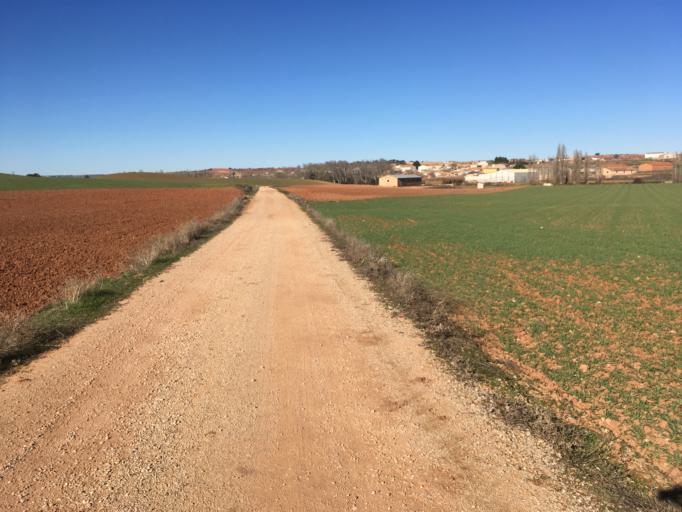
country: ES
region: Castille-La Mancha
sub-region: Provincia de Cuenca
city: Atalaya del Canavate
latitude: 39.5429
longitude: -2.2446
